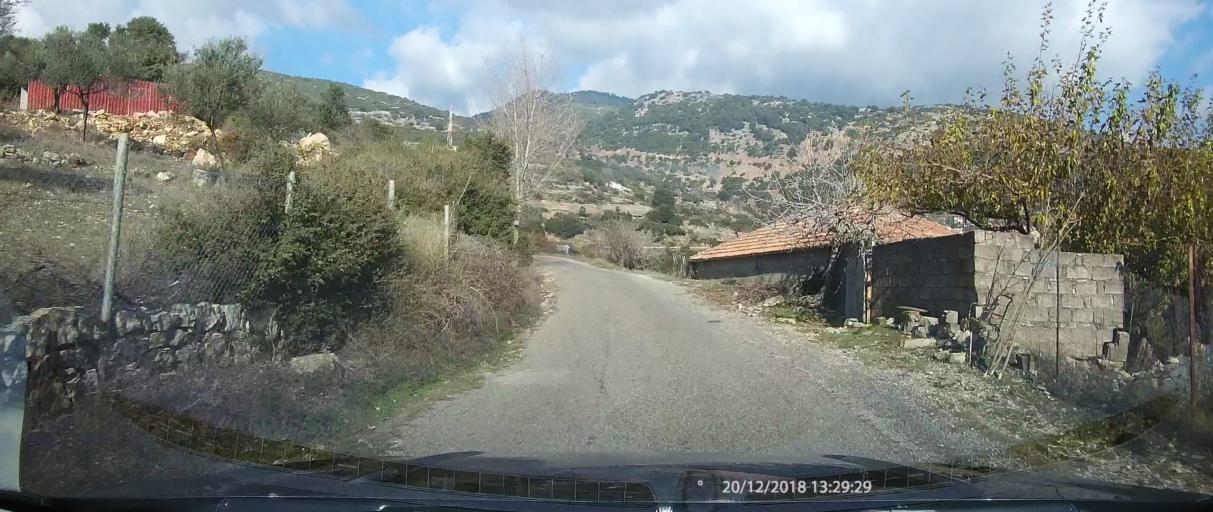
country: GR
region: West Greece
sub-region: Nomos Aitolias kai Akarnanias
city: Paravola
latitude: 38.6295
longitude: 21.5798
